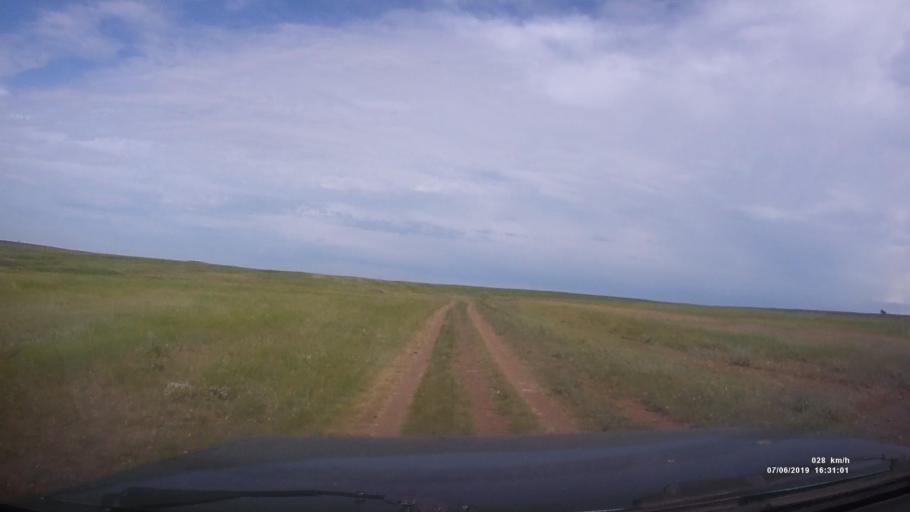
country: RU
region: Rostov
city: Staraya Stanitsa
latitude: 48.2556
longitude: 40.3264
